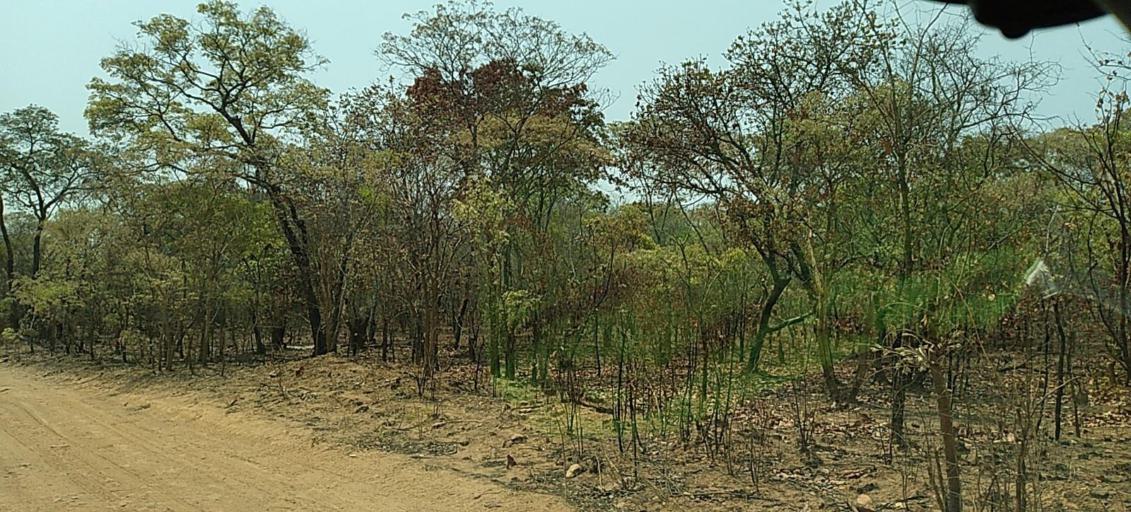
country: ZM
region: North-Western
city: Kabompo
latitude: -13.7133
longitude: 24.3269
